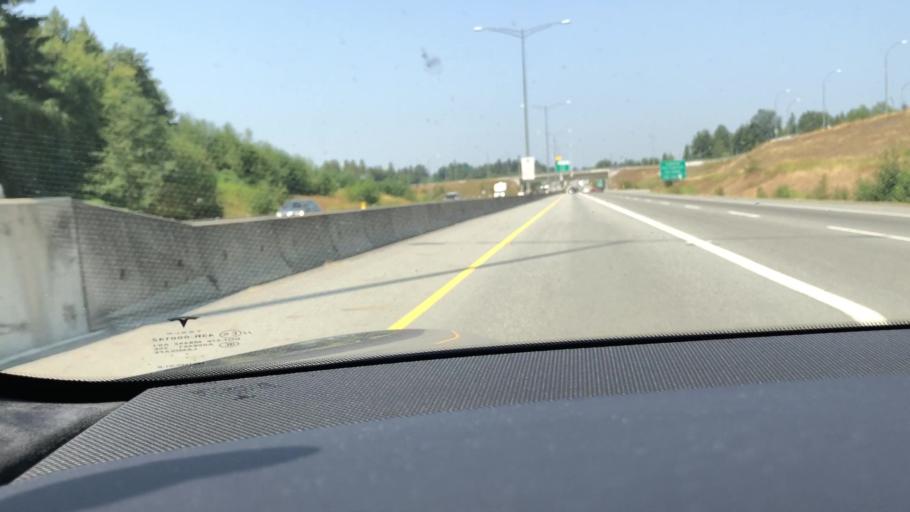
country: CA
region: British Columbia
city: Pitt Meadows
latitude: 49.1895
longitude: -122.7676
